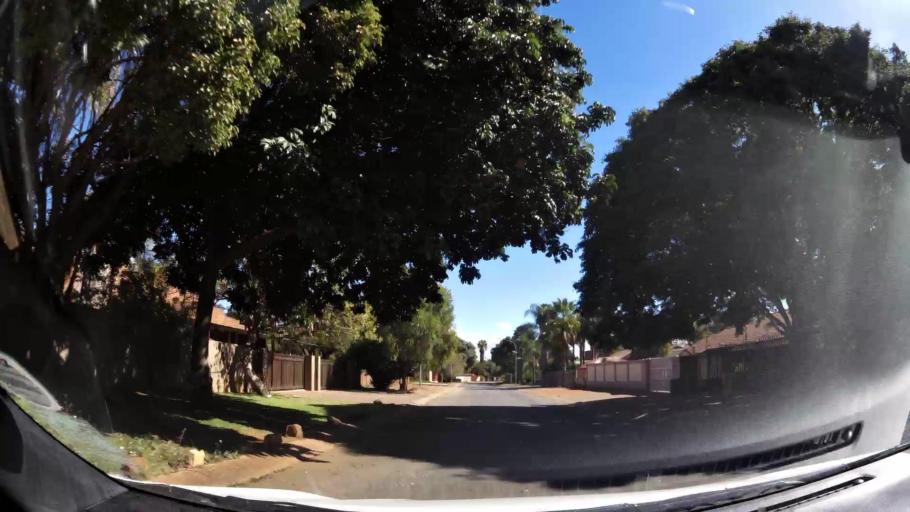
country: ZA
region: Limpopo
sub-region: Capricorn District Municipality
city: Polokwane
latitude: -23.9126
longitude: 29.4897
